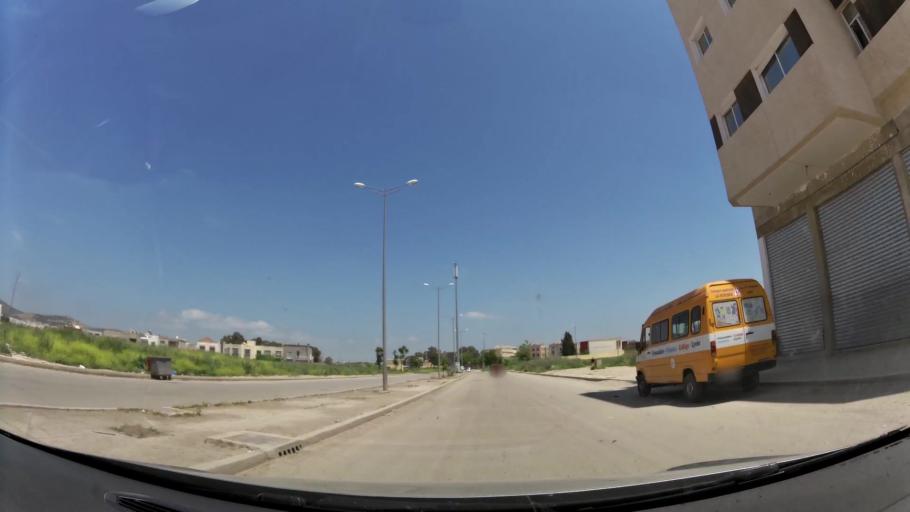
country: MA
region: Fes-Boulemane
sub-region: Fes
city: Fes
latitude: 34.0367
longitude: -5.0441
